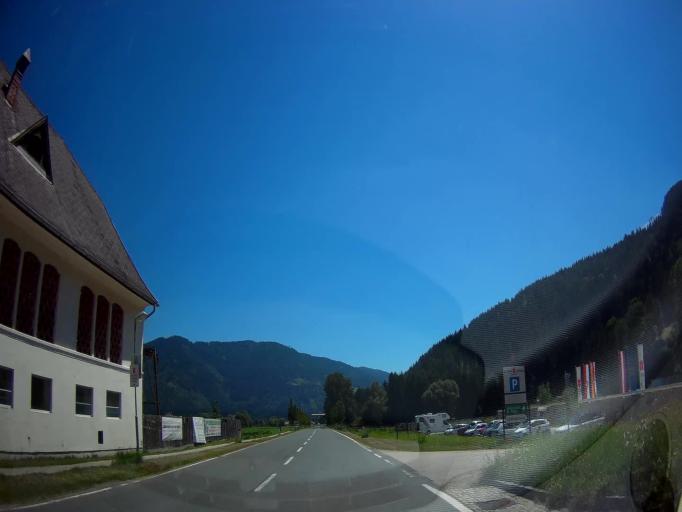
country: AT
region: Carinthia
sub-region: Politischer Bezirk Sankt Veit an der Glan
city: Friesach
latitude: 46.9459
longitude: 14.4132
